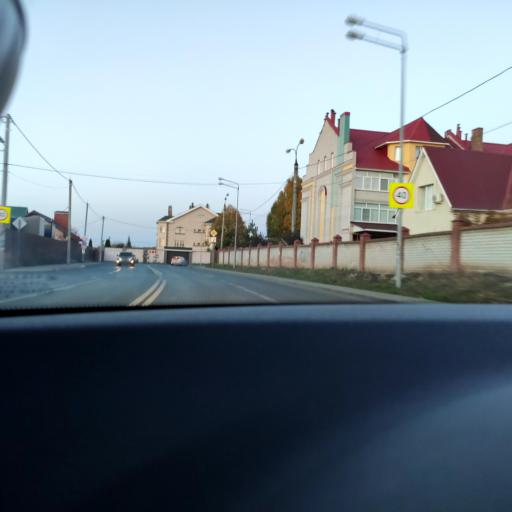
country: RU
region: Samara
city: Samara
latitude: 53.2697
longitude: 50.2160
